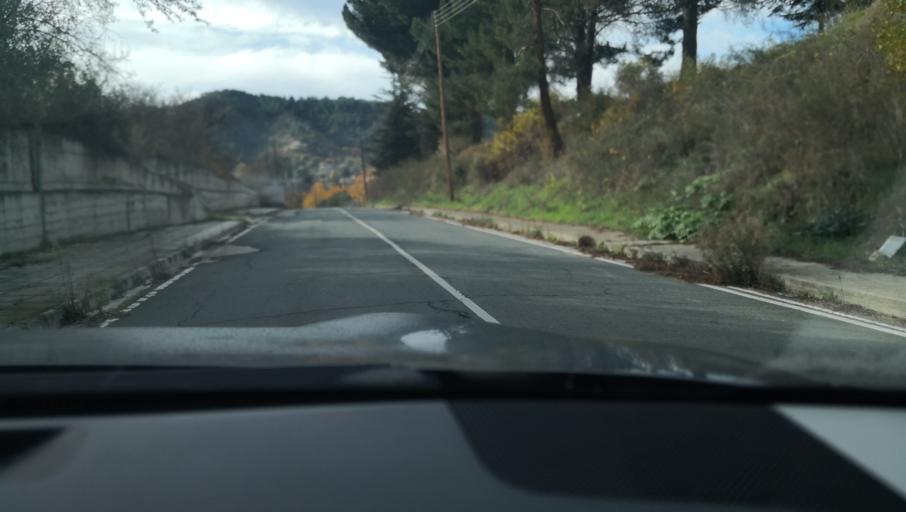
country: CY
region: Lefkosia
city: Lefka
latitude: 35.0295
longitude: 32.7288
